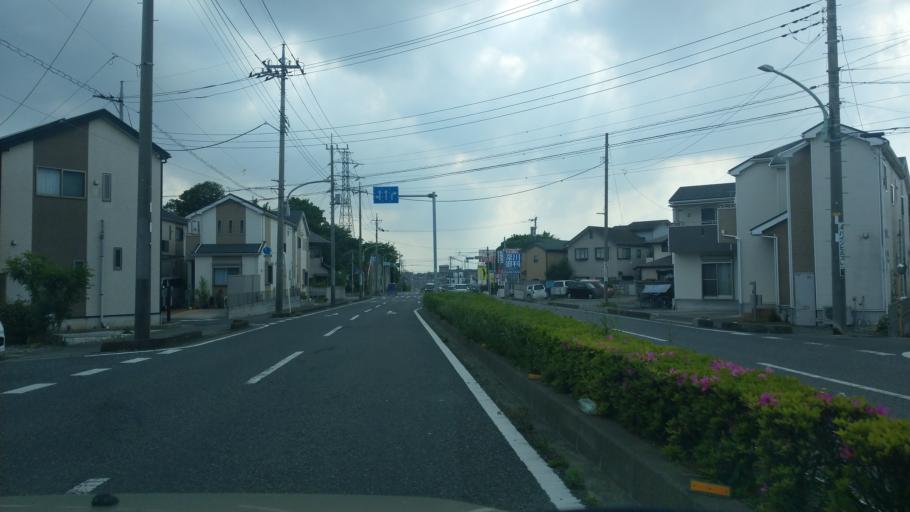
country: JP
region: Saitama
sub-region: Kawaguchi-shi
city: Hatogaya-honcho
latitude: 35.8633
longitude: 139.7211
